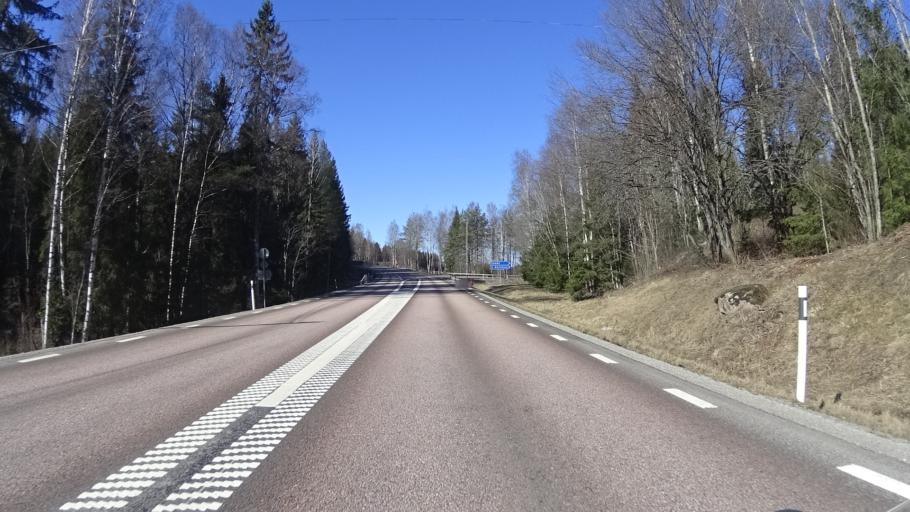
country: SE
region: Vaermland
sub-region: Sunne Kommun
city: Sunne
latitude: 59.6535
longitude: 12.9446
